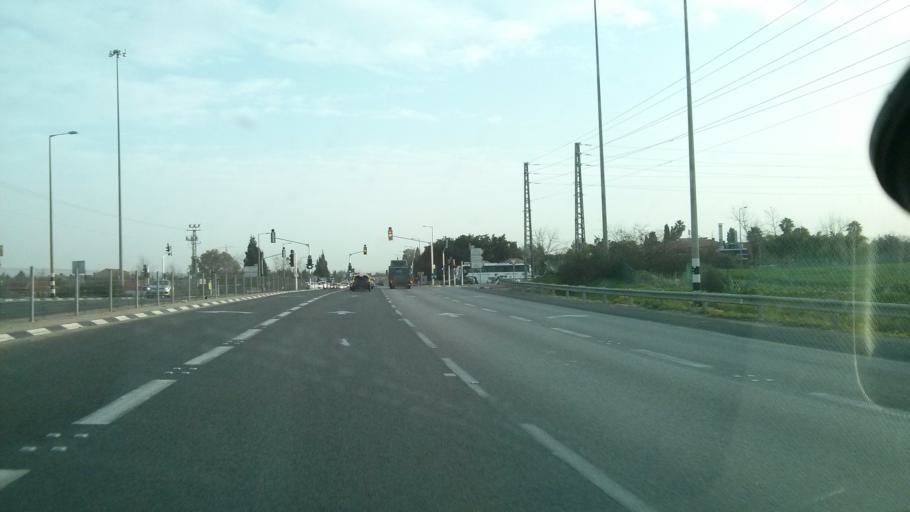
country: PS
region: West Bank
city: Nazlat `Isa
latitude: 32.4642
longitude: 34.9929
